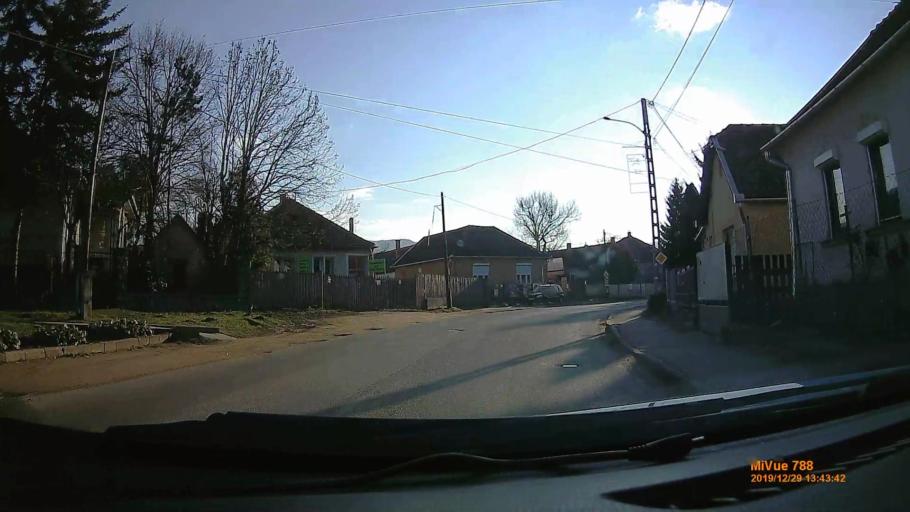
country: HU
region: Heves
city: Recsk
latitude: 47.9330
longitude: 20.1065
